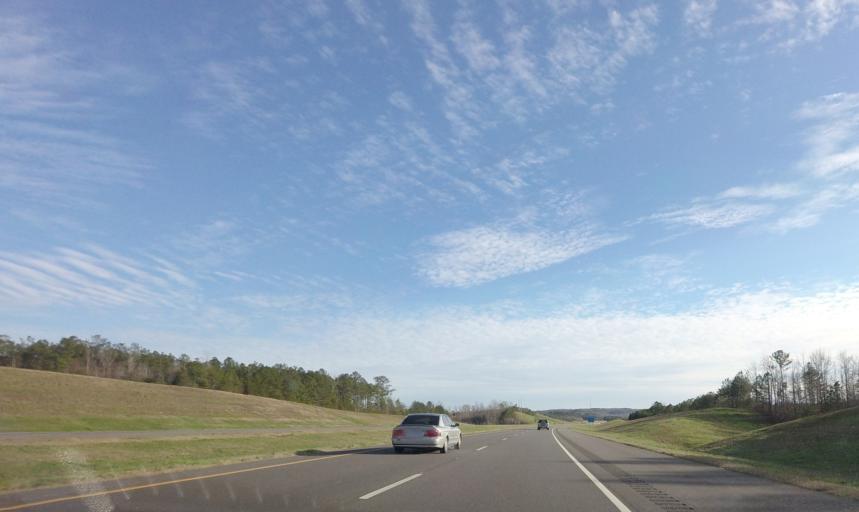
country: US
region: Alabama
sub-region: Walker County
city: Jasper
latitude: 33.8292
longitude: -87.3190
